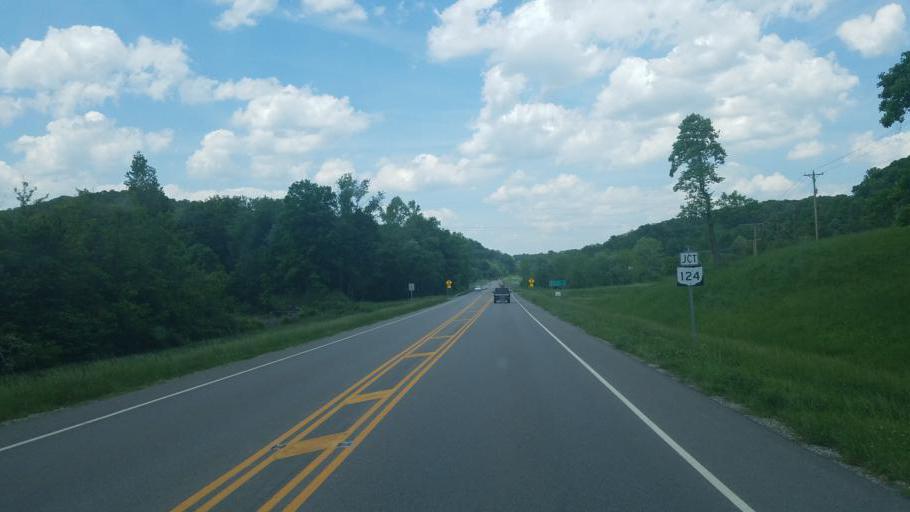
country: US
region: Ohio
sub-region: Meigs County
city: Middleport
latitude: 39.0210
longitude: -82.0670
